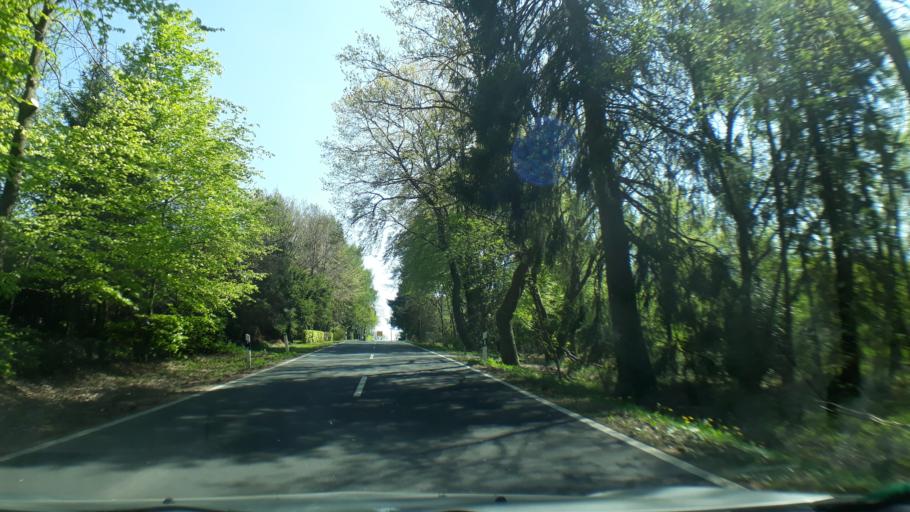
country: DE
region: North Rhine-Westphalia
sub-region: Regierungsbezirk Koln
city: Simmerath
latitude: 50.6440
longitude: 6.2642
